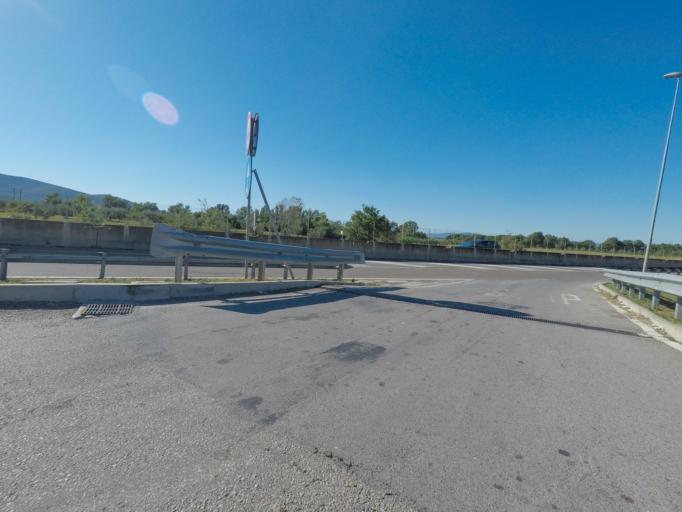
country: IT
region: Tuscany
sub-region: Provincia di Grosseto
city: Grosseto
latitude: 42.6752
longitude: 11.1414
